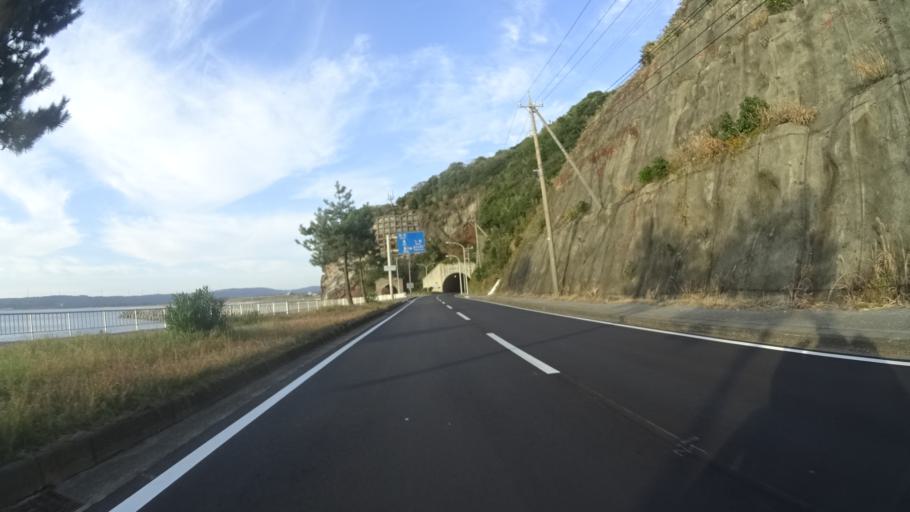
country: JP
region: Ishikawa
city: Nanao
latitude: 37.1309
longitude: 136.7270
